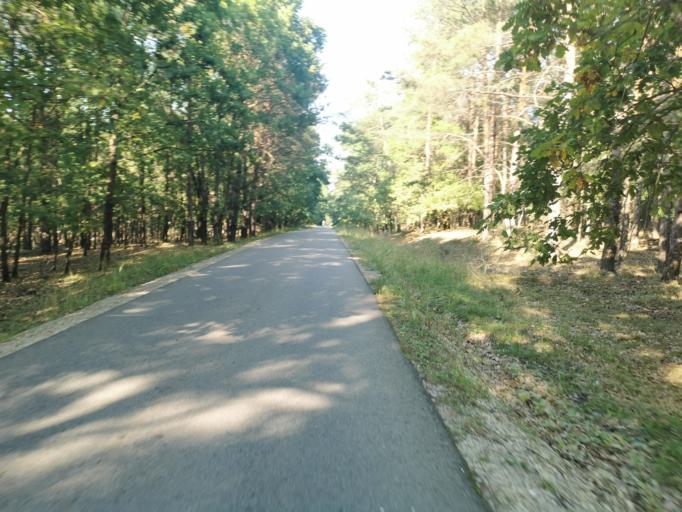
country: SK
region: Trnavsky
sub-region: Okres Senica
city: Senica
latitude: 48.6434
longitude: 17.2669
